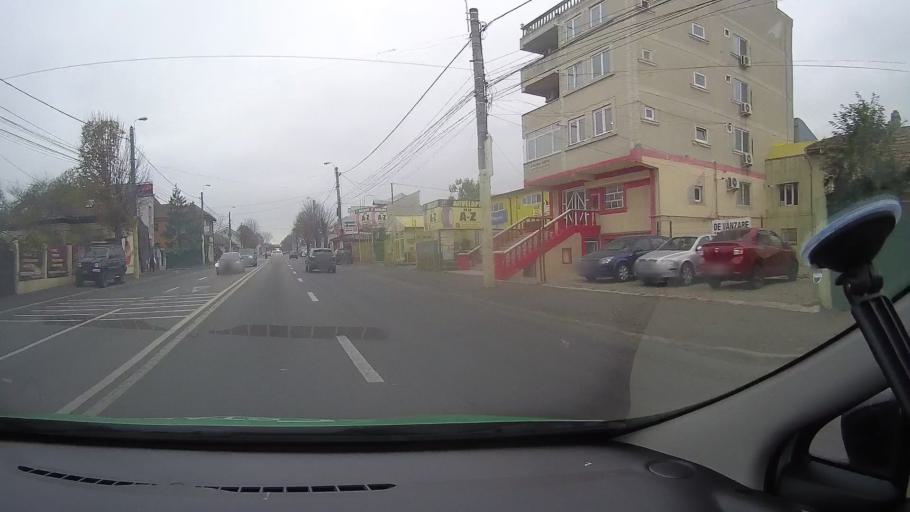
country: RO
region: Constanta
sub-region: Municipiul Constanta
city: Constanta
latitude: 44.1702
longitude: 28.6000
